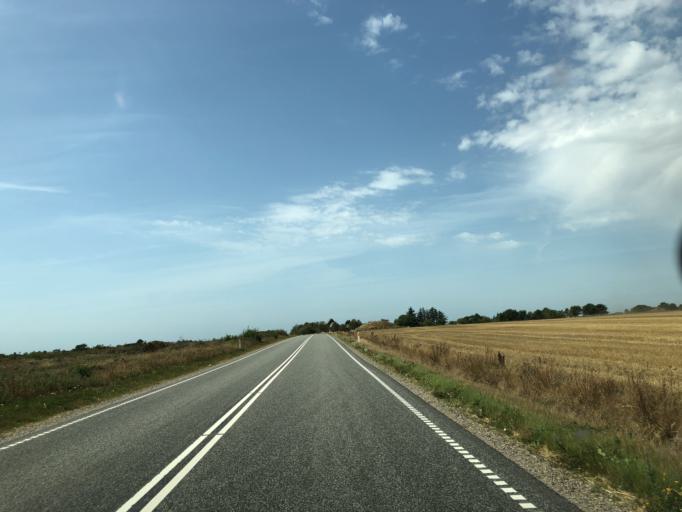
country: DK
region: Central Jutland
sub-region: Ringkobing-Skjern Kommune
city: Skjern
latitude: 56.0311
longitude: 8.4569
